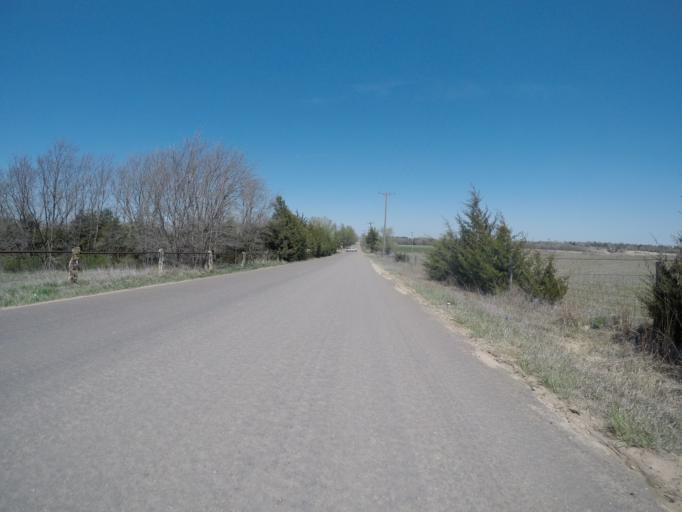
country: US
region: Kansas
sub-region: Pratt County
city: Pratt
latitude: 37.6324
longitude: -98.7670
